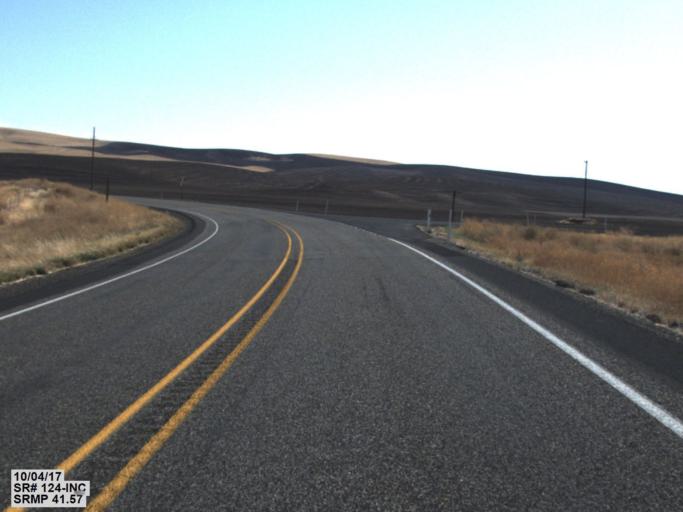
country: US
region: Washington
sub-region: Walla Walla County
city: Waitsburg
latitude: 46.2686
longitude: -118.2207
